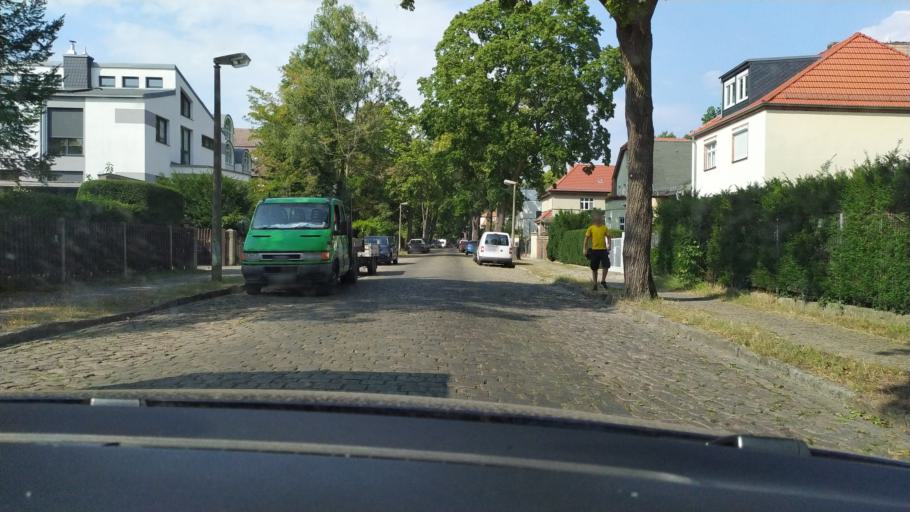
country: DE
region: Berlin
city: Grunau
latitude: 52.4170
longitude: 13.5929
